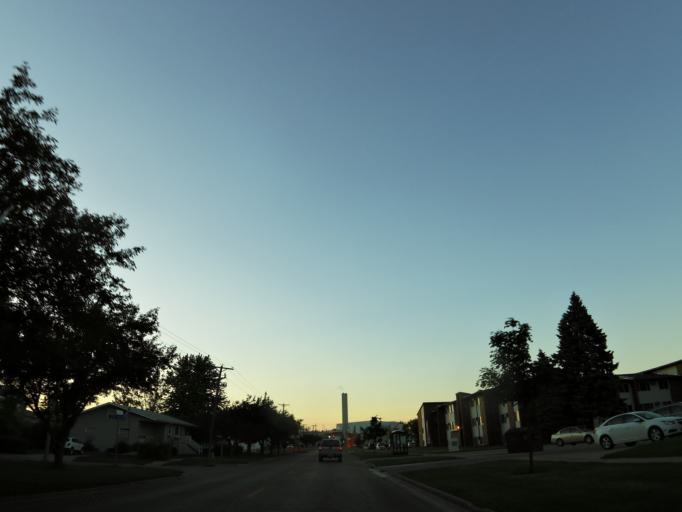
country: US
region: North Dakota
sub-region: Grand Forks County
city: Grand Forks
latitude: 47.9301
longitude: -97.0811
